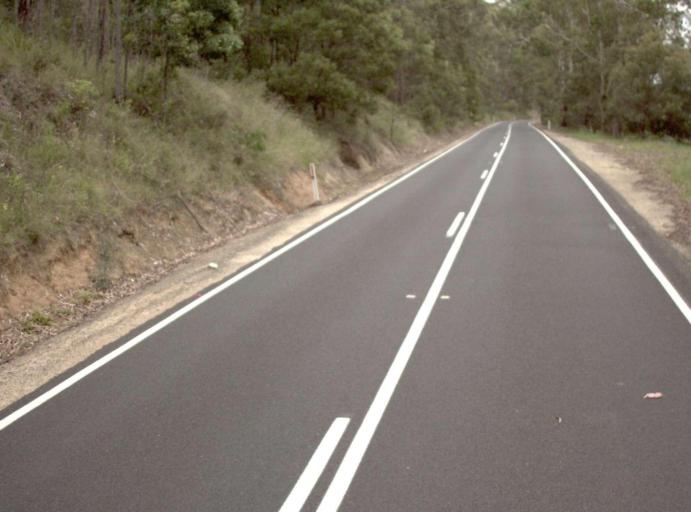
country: AU
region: New South Wales
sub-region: Bombala
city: Bombala
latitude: -37.4505
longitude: 149.1932
